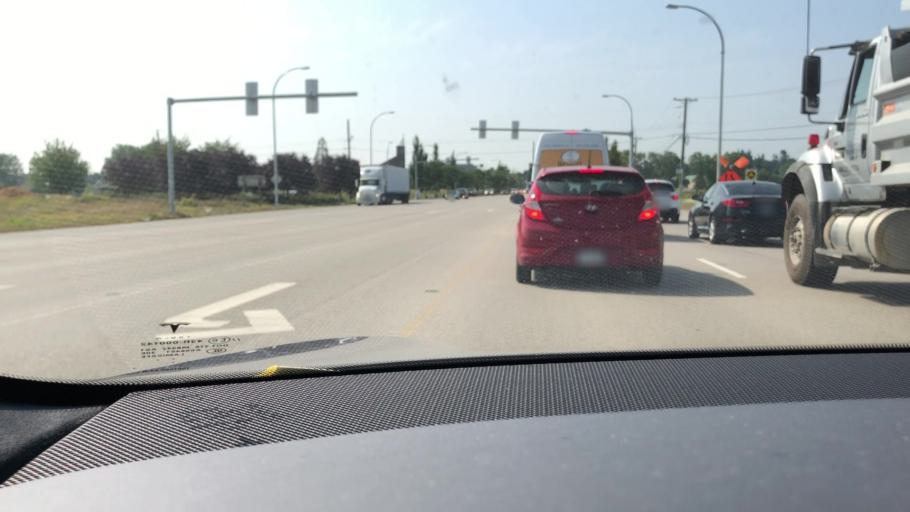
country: CA
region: British Columbia
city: Ladner
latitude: 49.0422
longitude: -123.0688
